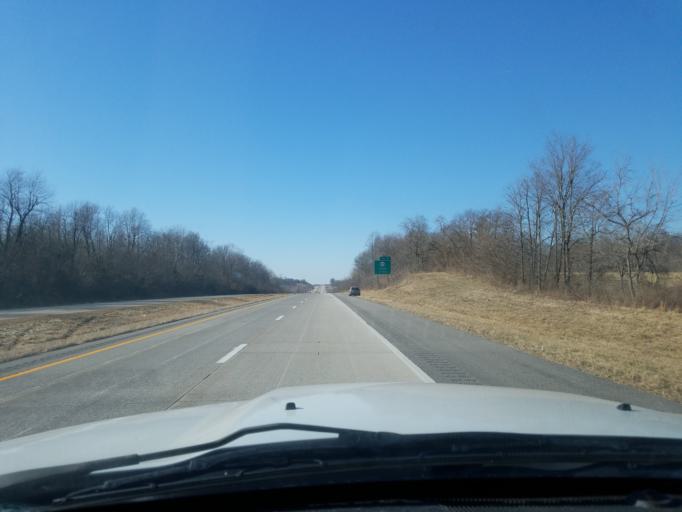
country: US
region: Kentucky
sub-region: Henderson County
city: Henderson
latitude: 37.7777
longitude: -87.4463
